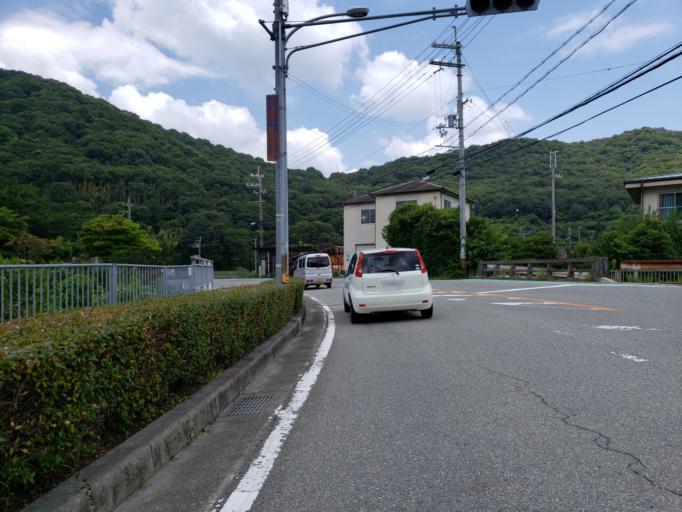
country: JP
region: Hyogo
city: Aioi
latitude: 34.7863
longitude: 134.4793
